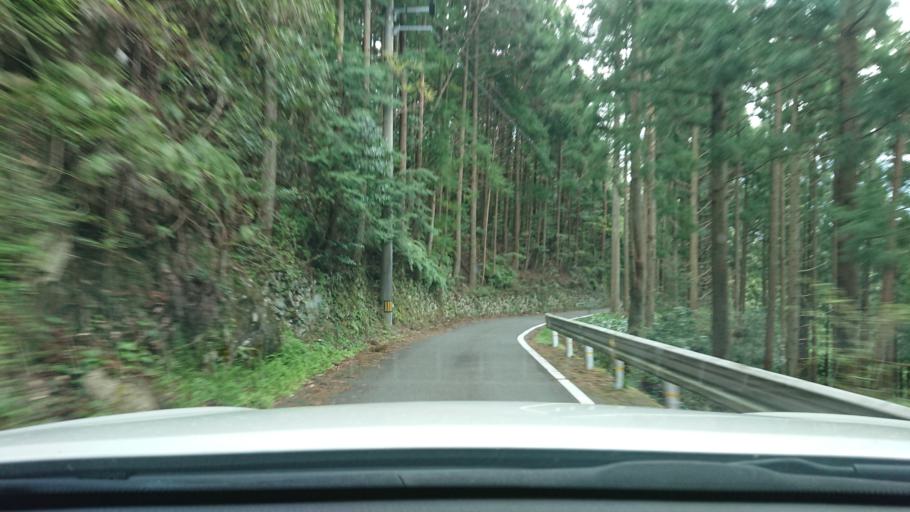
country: JP
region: Tokushima
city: Kamojimacho-jogejima
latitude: 33.8836
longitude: 134.3819
